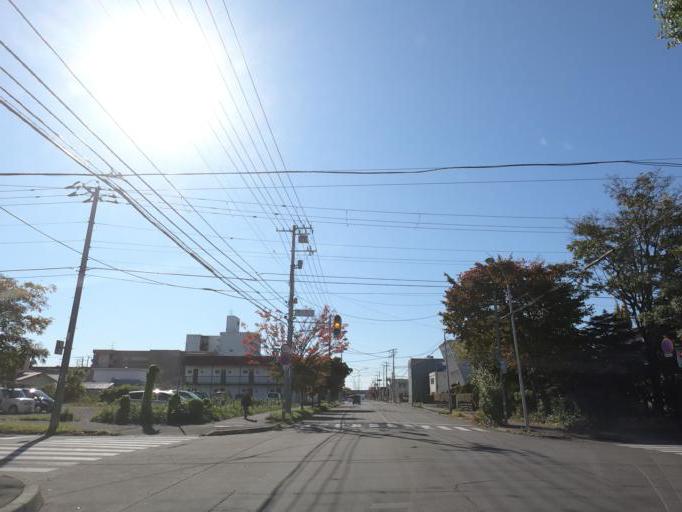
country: JP
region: Hokkaido
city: Obihiro
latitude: 42.9189
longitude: 143.2120
